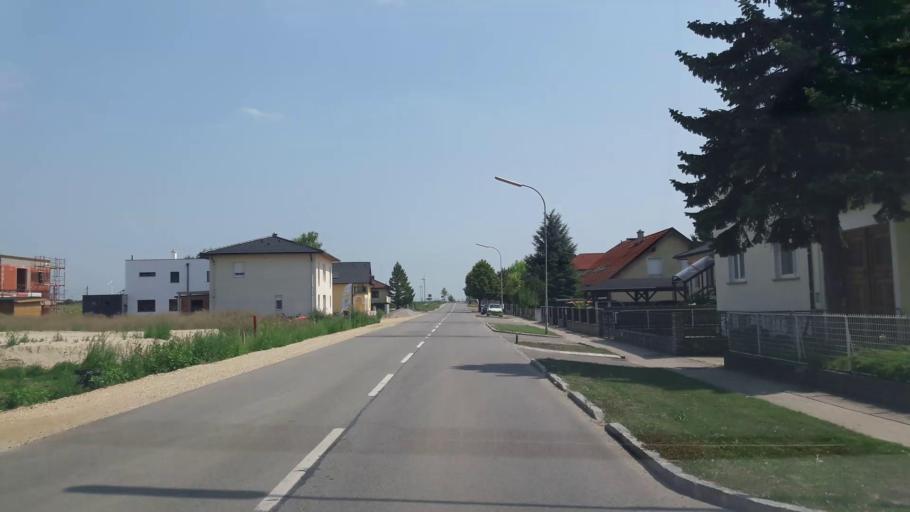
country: AT
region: Lower Austria
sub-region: Politischer Bezirk Bruck an der Leitha
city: Trautmannsdorf an der Leitha
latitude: 48.0226
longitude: 16.6504
